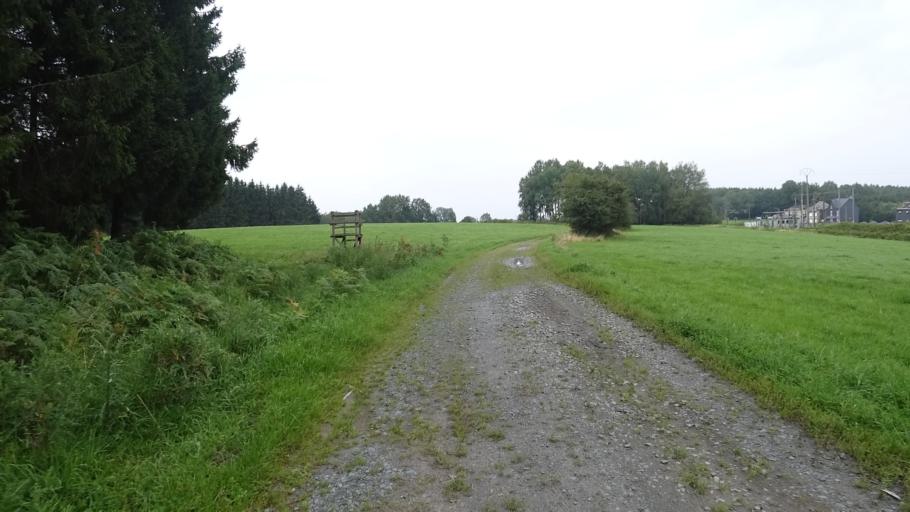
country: BE
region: Wallonia
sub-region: Province du Luxembourg
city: Chiny
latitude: 49.7942
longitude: 5.3284
